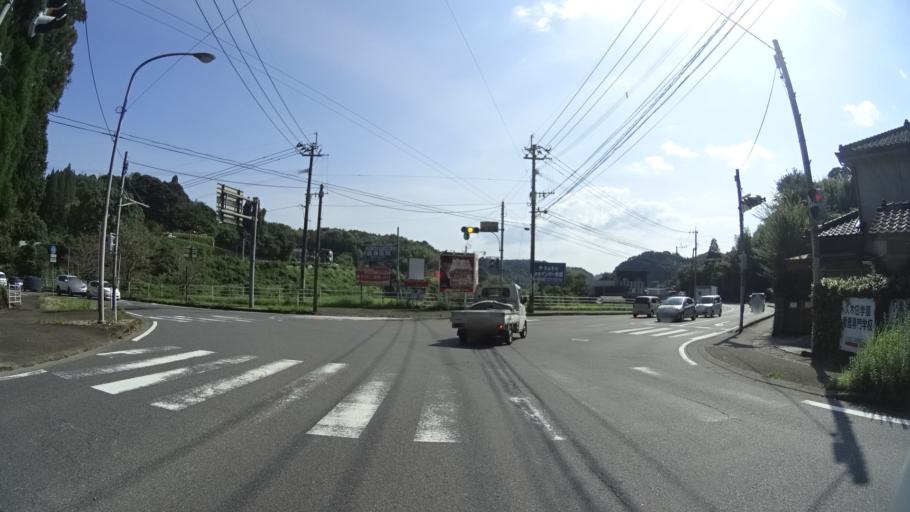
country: JP
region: Kagoshima
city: Kagoshima-shi
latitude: 31.6711
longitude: 130.5621
